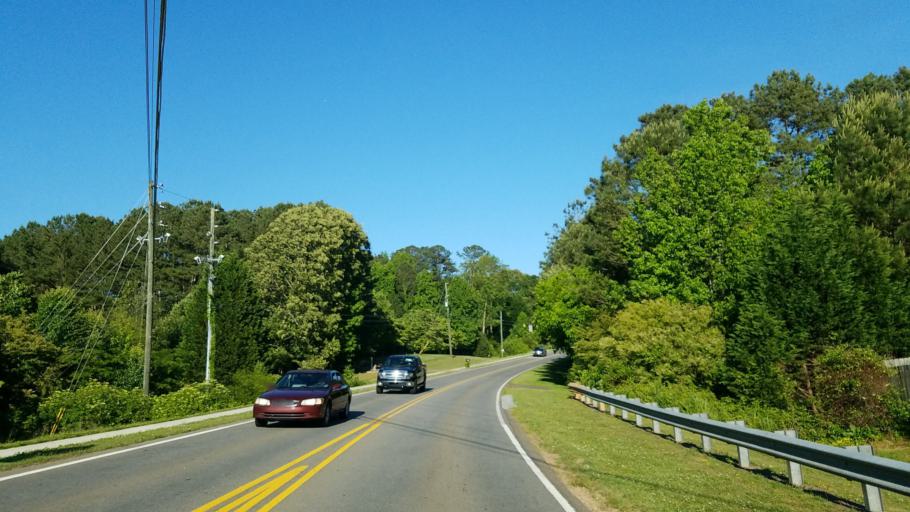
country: US
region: Georgia
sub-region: Cherokee County
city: Holly Springs
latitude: 34.1714
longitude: -84.4703
